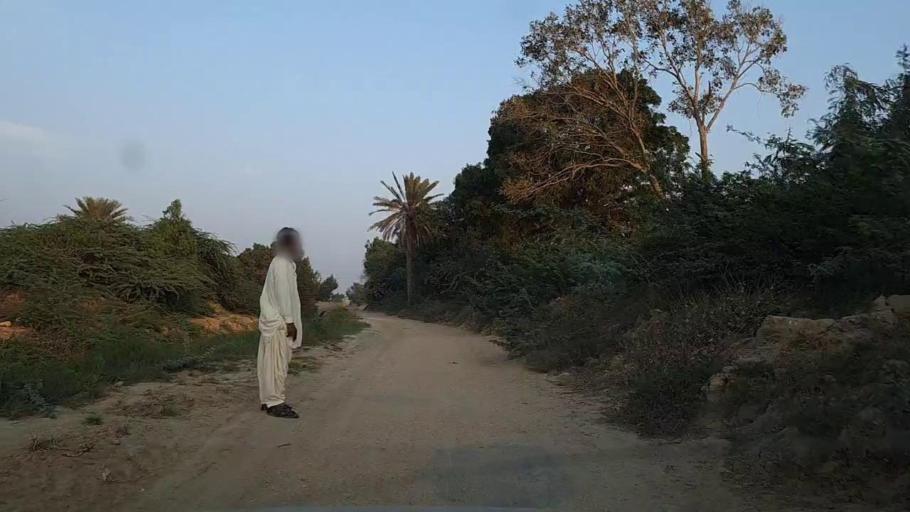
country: PK
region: Sindh
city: Mirpur Sakro
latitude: 24.6110
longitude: 67.6004
